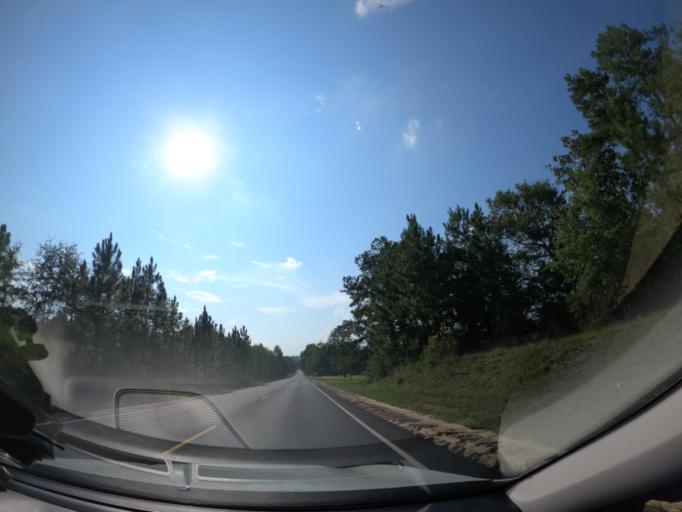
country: US
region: South Carolina
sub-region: Aiken County
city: Jackson
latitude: 33.4054
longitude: -81.7795
